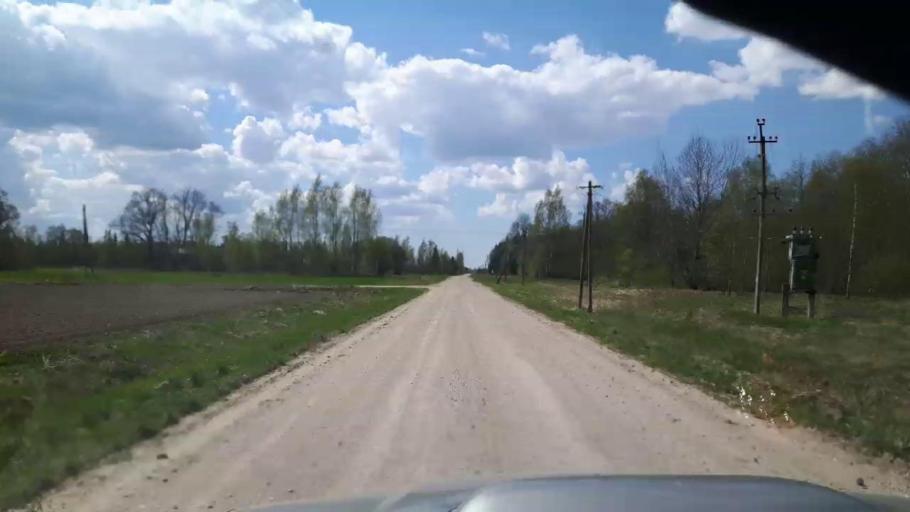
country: EE
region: Paernumaa
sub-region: Tootsi vald
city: Tootsi
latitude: 58.4703
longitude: 24.8985
